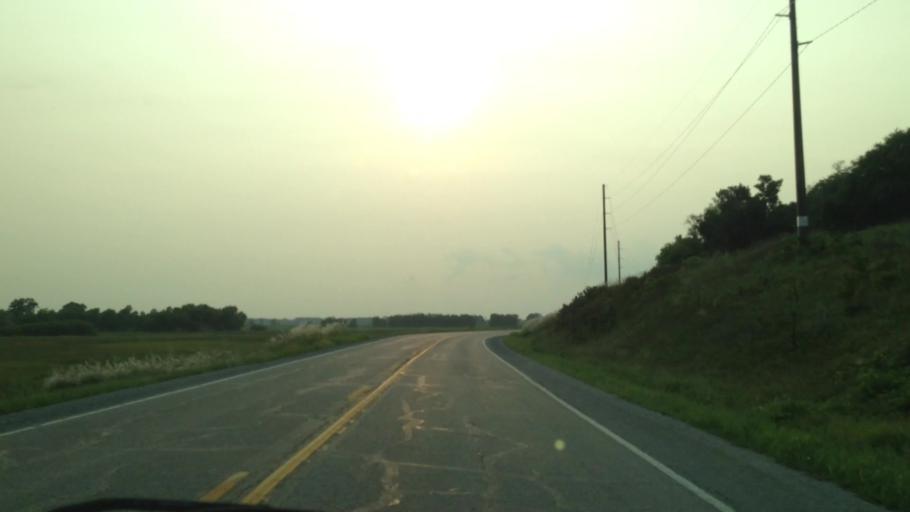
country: US
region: Iowa
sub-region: Benton County
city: Walford
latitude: 41.7982
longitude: -91.9267
